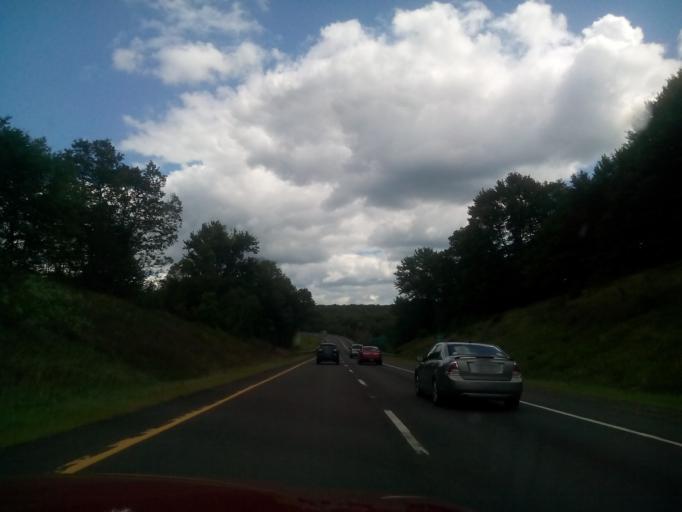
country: US
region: Pennsylvania
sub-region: Luzerne County
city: White Haven
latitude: 41.0571
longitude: -75.7312
